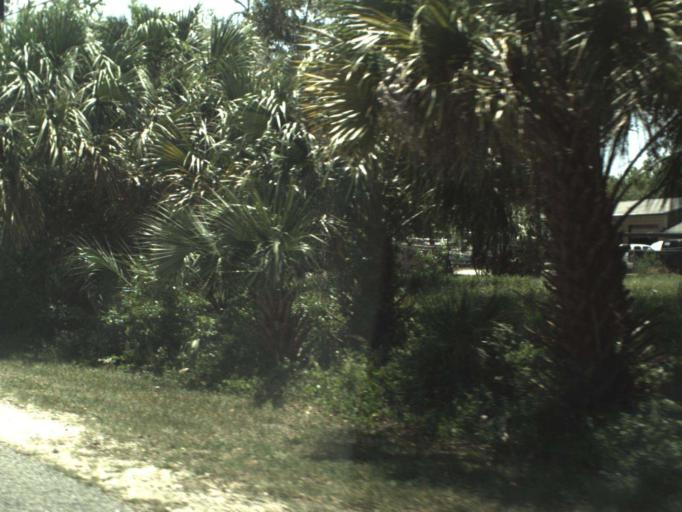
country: US
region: Florida
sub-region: Volusia County
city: Oak Hill
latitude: 28.9059
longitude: -80.8656
